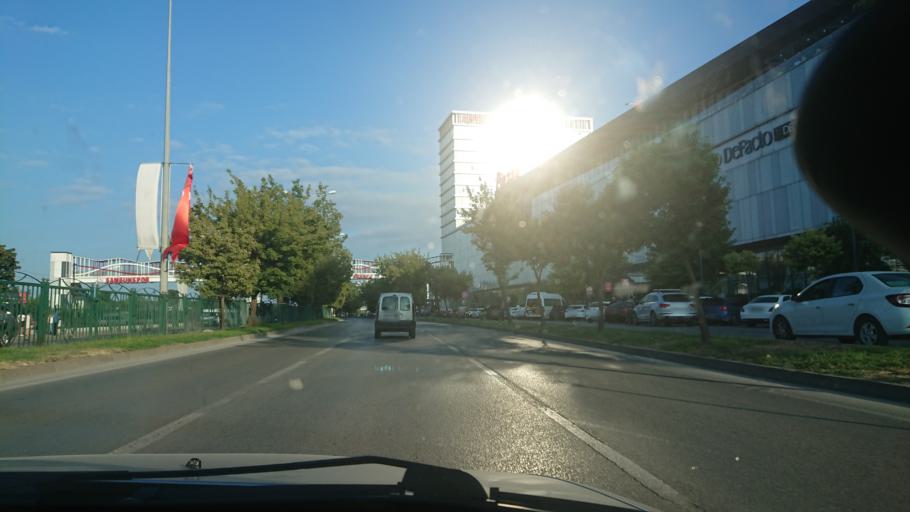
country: TR
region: Samsun
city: Samsun
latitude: 41.2774
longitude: 36.3536
